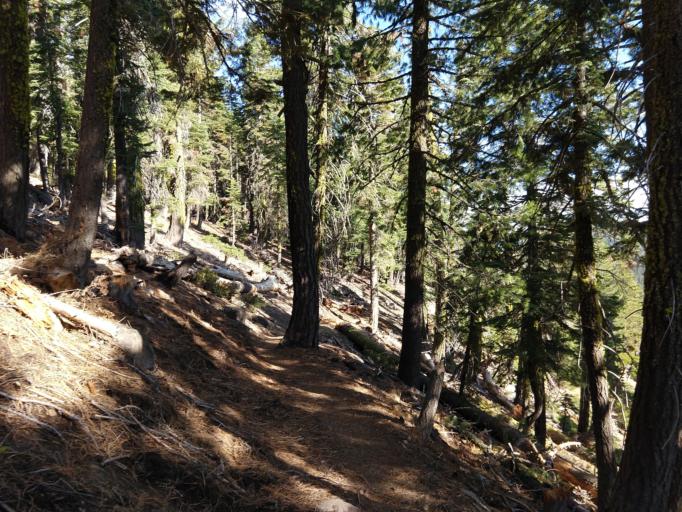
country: US
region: California
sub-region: Plumas County
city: Chester
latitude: 40.4469
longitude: -121.4006
